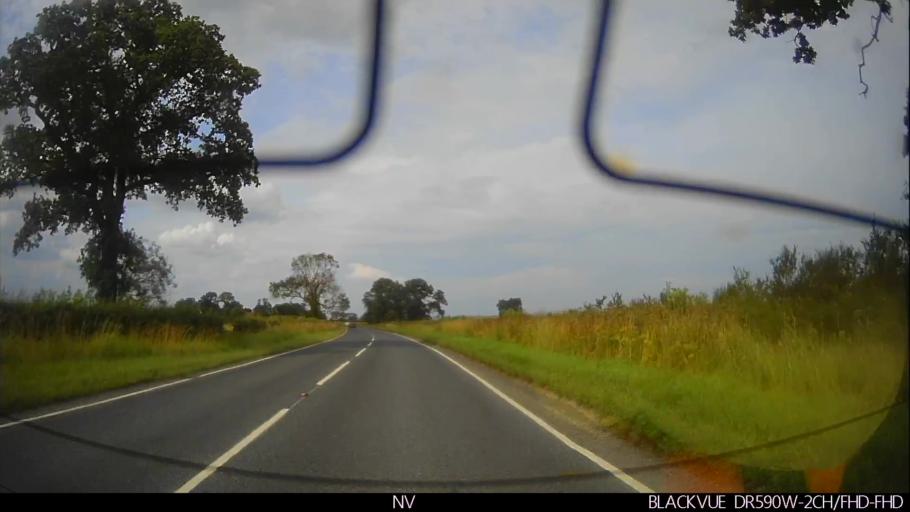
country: GB
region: England
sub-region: North Yorkshire
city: Malton
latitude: 54.1638
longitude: -0.7669
